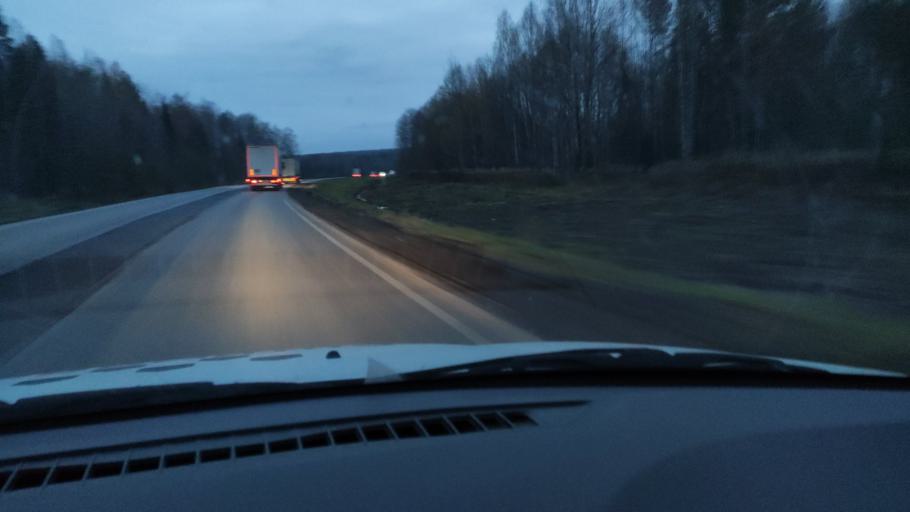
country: RU
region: Kirov
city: Kostino
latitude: 58.8288
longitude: 53.3863
